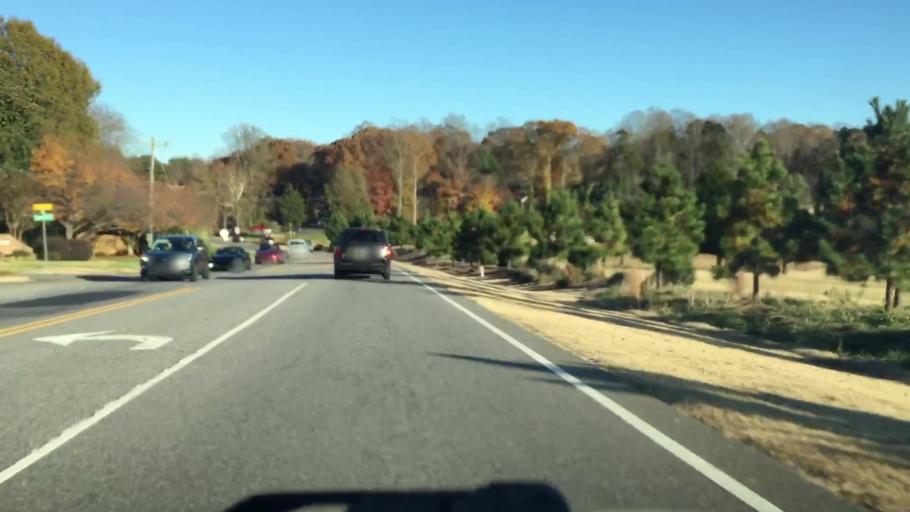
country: US
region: North Carolina
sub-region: Iredell County
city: Mooresville
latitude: 35.5797
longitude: -80.8356
